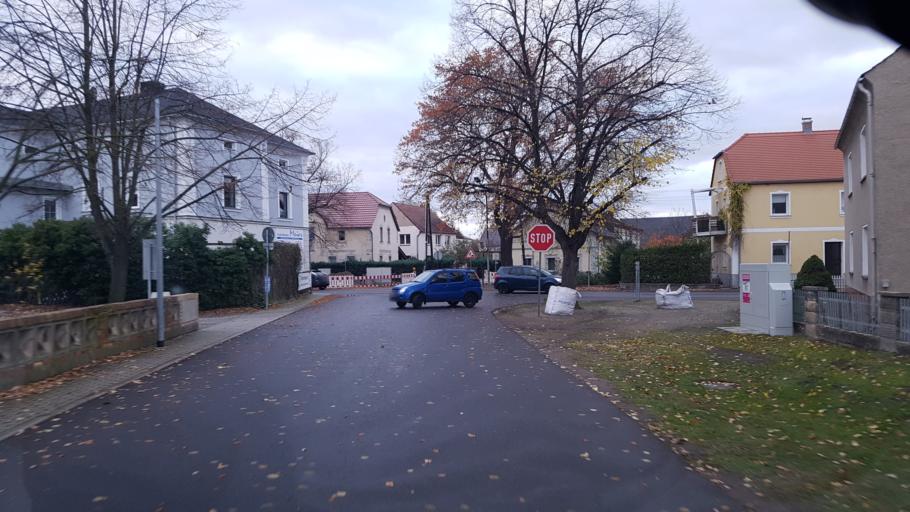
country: DE
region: Brandenburg
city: Ortrand
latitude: 51.3787
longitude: 13.7586
